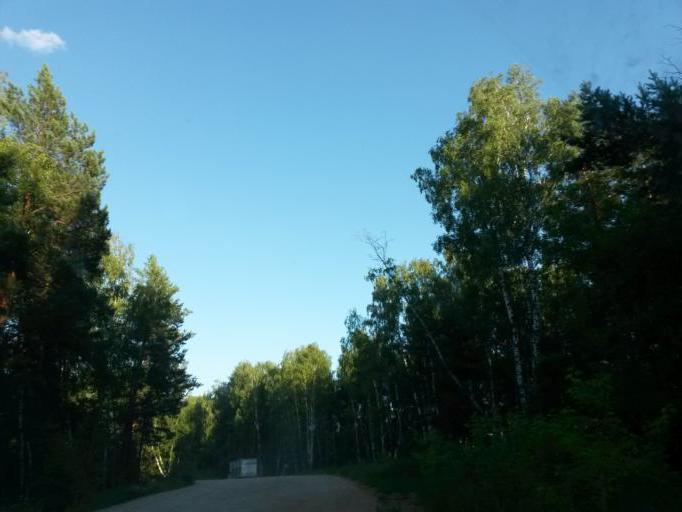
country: RU
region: Moskovskaya
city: Protvino
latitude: 54.8826
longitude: 37.2913
